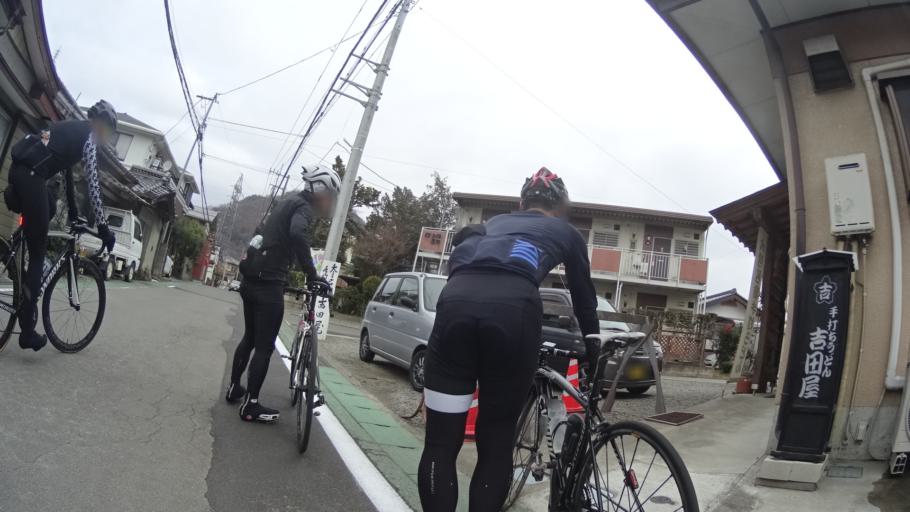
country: JP
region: Yamanashi
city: Otsuki
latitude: 35.6136
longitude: 138.9412
